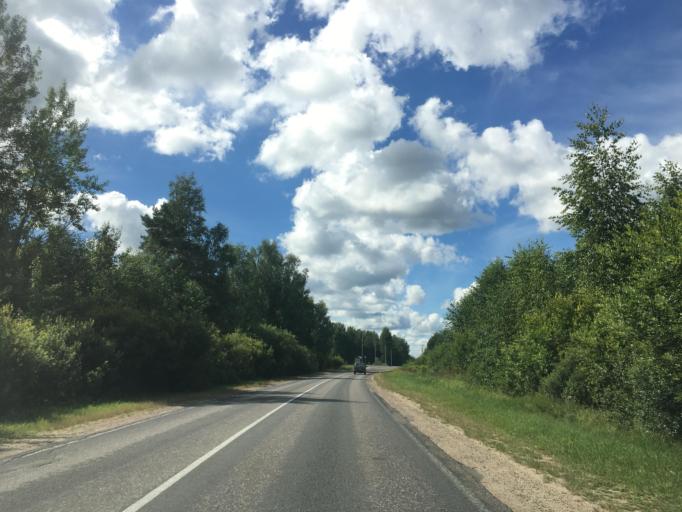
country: RU
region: Pskov
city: Pskov
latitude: 57.6932
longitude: 28.1783
